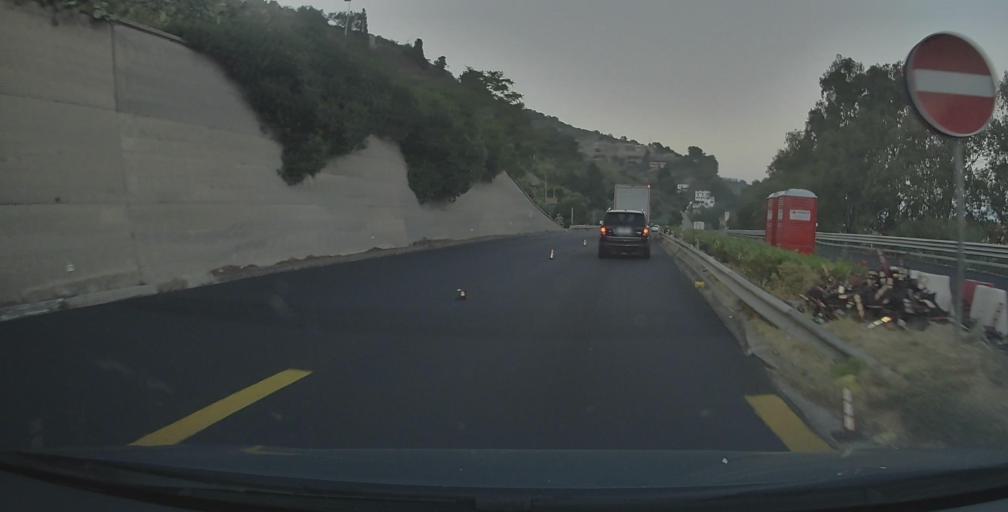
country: IT
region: Sicily
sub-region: Messina
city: Guidomandri Marina
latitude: 38.0366
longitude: 15.4514
